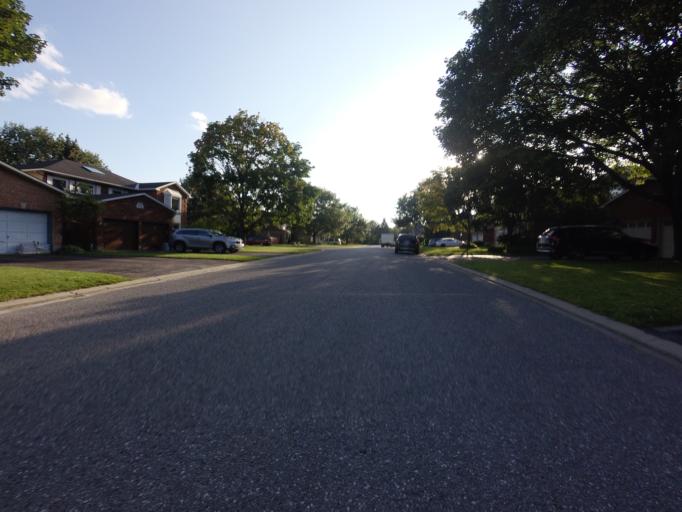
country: CA
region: Ontario
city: Bells Corners
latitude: 45.3412
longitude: -75.7733
